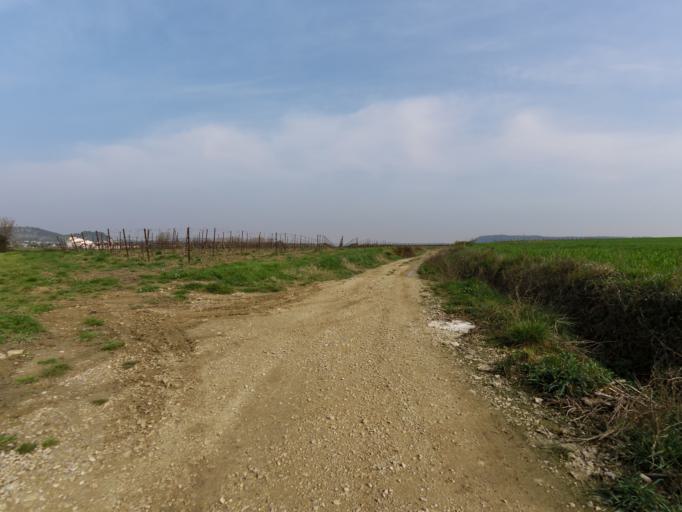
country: FR
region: Languedoc-Roussillon
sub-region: Departement du Gard
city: Calvisson
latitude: 43.7667
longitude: 4.2040
